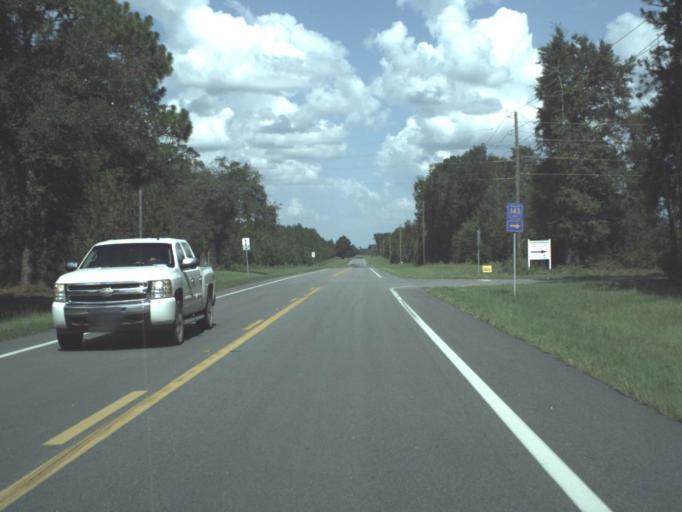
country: US
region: Florida
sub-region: Madison County
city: Madison
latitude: 30.4866
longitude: -83.2079
